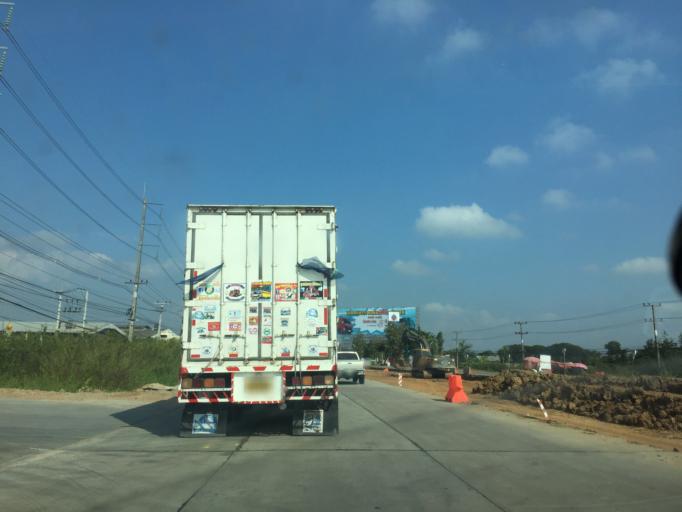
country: TH
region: Chiang Mai
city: Saraphi
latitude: 18.6975
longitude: 99.0488
